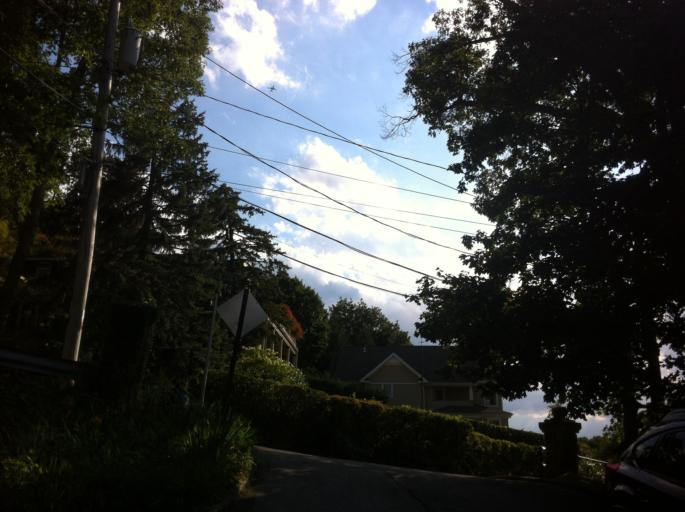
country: US
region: New York
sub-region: Nassau County
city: Sea Cliff
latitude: 40.8508
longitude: -73.6495
